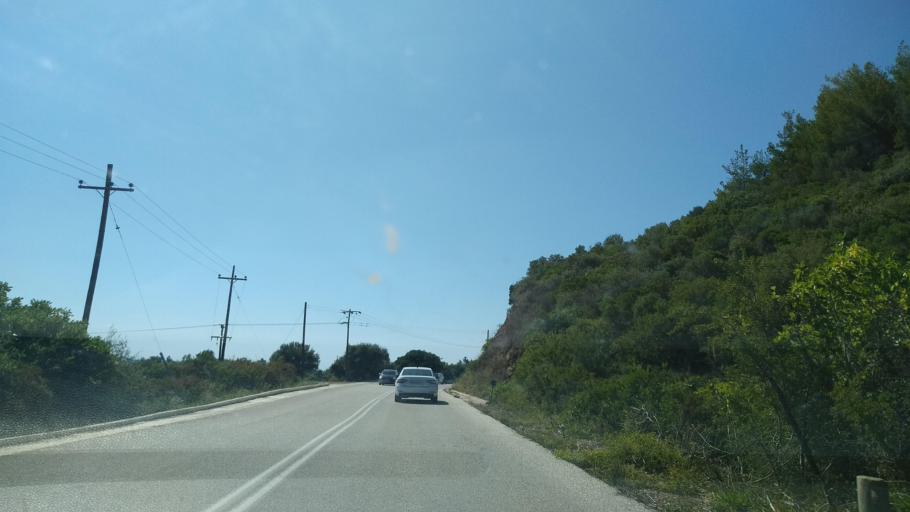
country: GR
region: Central Macedonia
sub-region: Nomos Chalkidikis
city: Sykia
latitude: 39.9807
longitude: 23.9133
